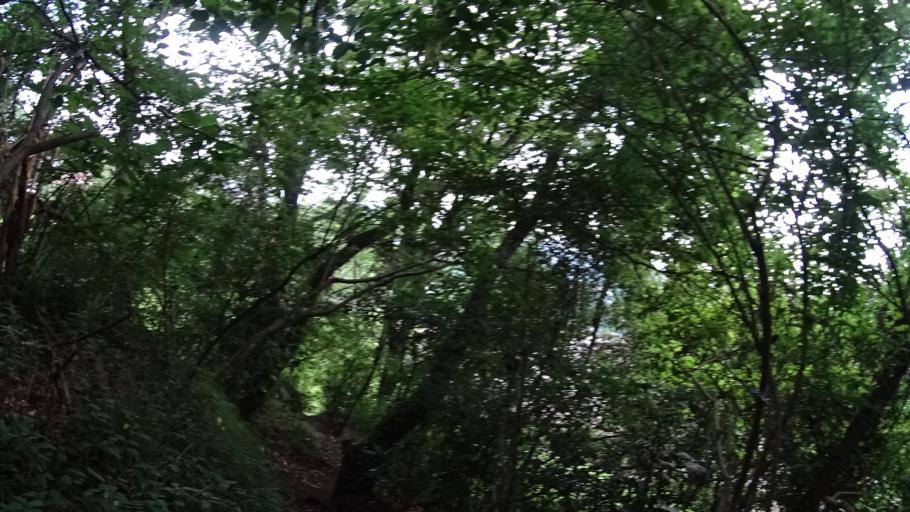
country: JP
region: Kanagawa
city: Zushi
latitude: 35.3095
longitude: 139.6118
